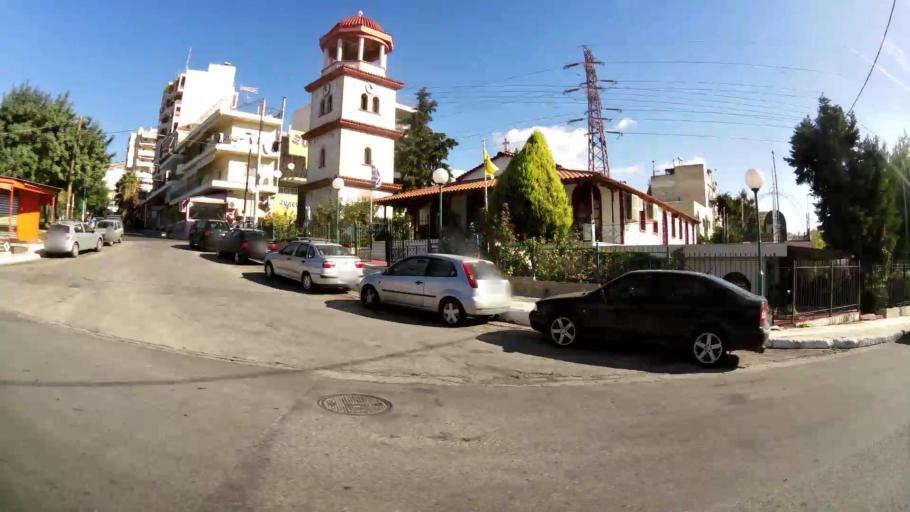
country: GR
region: Attica
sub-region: Nomos Piraios
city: Keratsini
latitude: 37.9653
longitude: 23.6121
